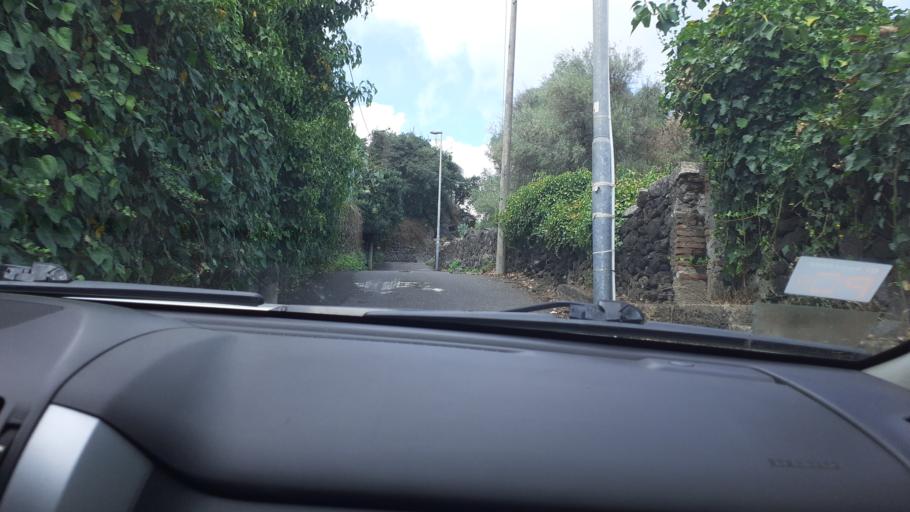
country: IT
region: Sicily
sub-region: Catania
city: San Giovanni la Punta
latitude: 37.5915
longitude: 15.0839
